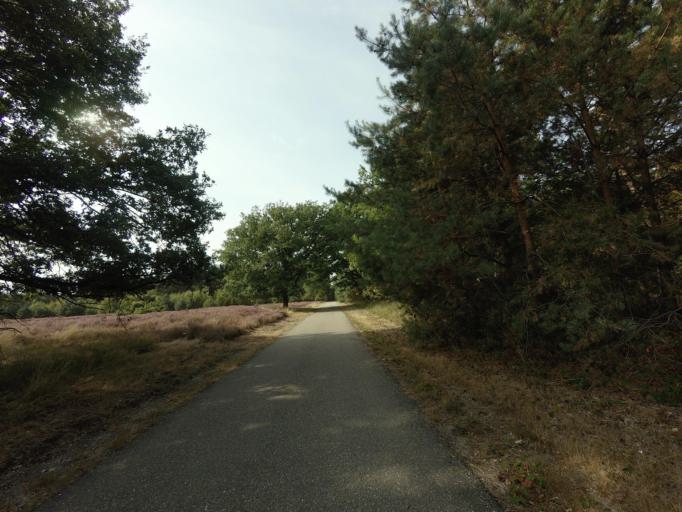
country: NL
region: North Brabant
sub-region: Gemeente Sint Anthonis
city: Sint Anthonis
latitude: 51.6259
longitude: 5.8255
